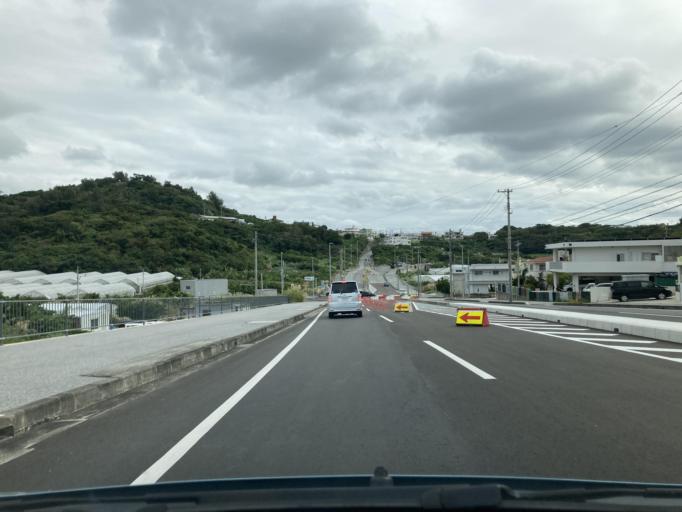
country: JP
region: Okinawa
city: Tomigusuku
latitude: 26.1670
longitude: 127.6778
